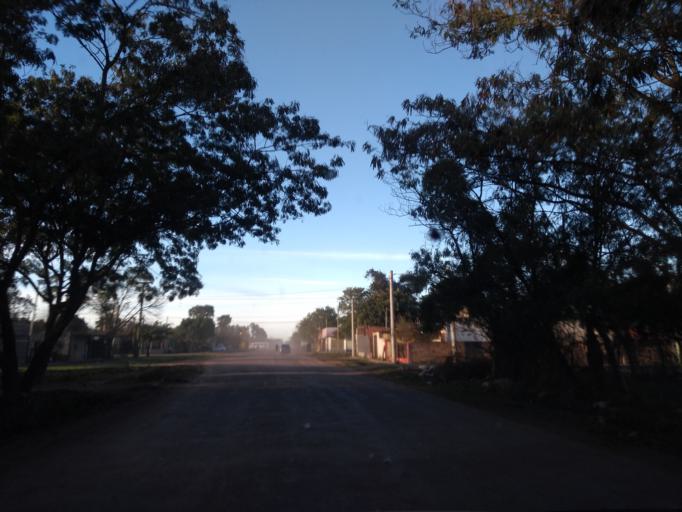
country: AR
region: Chaco
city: Resistencia
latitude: -27.4951
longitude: -58.9783
